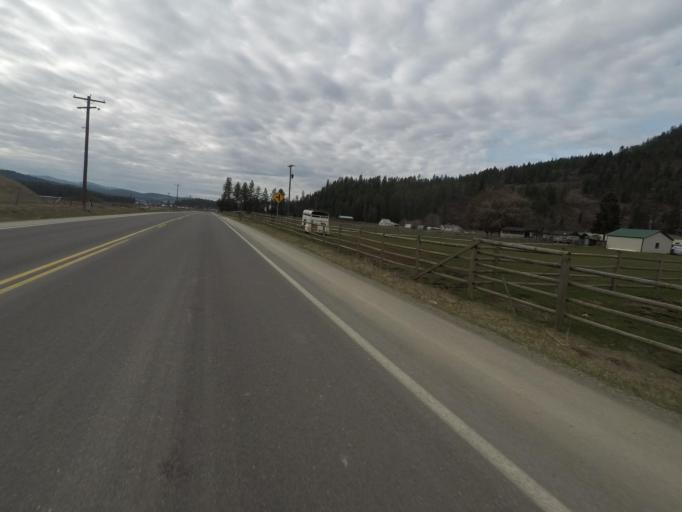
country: US
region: Washington
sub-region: Stevens County
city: Colville
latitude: 48.5715
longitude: -117.8793
